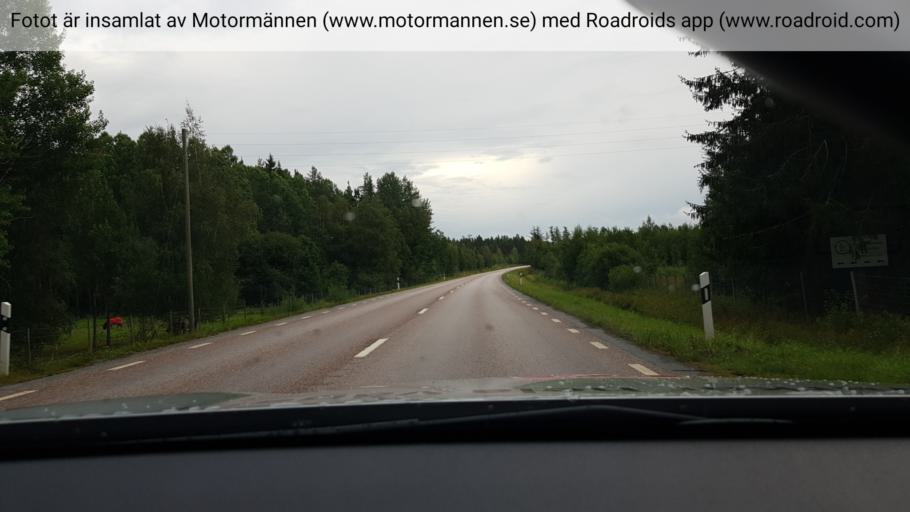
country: SE
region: Uppsala
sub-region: Osthammars Kommun
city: Osterbybruk
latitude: 60.4209
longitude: 17.8526
